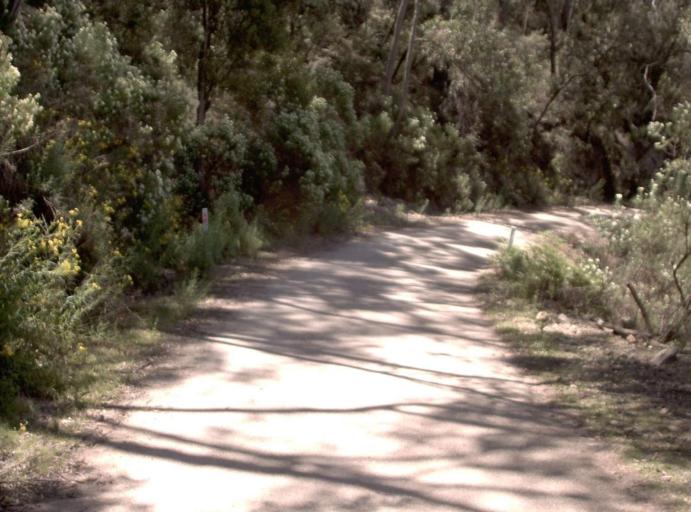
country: AU
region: New South Wales
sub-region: Snowy River
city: Jindabyne
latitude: -37.0815
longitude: 148.3353
